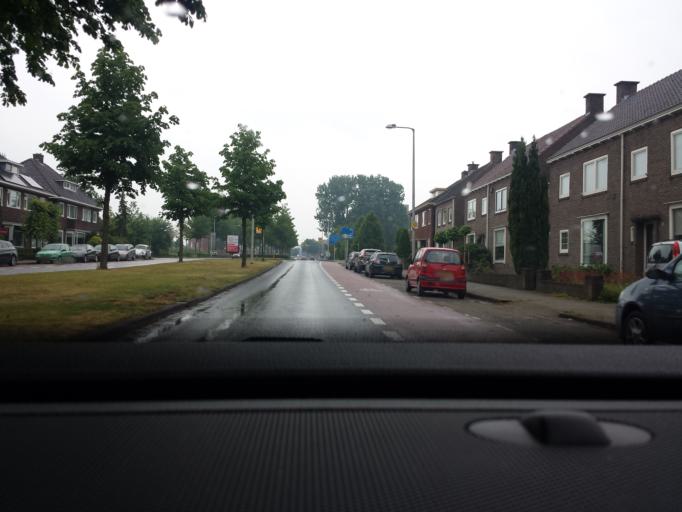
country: NL
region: Overijssel
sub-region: Gemeente Enschede
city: Enschede
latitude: 52.2105
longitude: 6.8849
